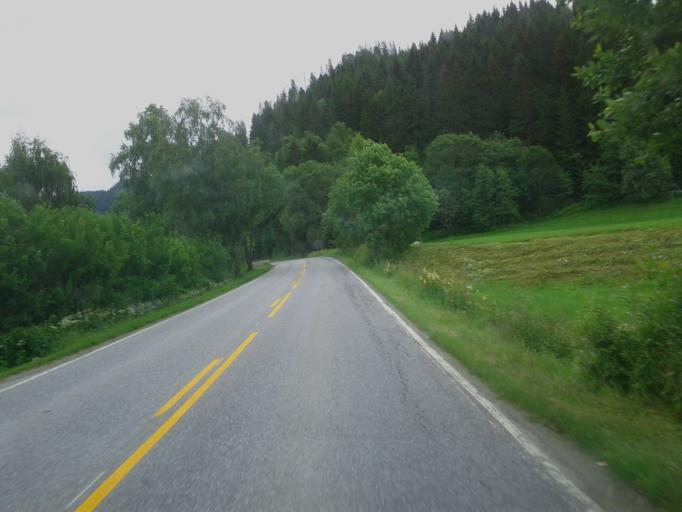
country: NO
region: Sor-Trondelag
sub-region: Midtre Gauldal
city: Storen
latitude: 63.0173
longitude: 10.3367
